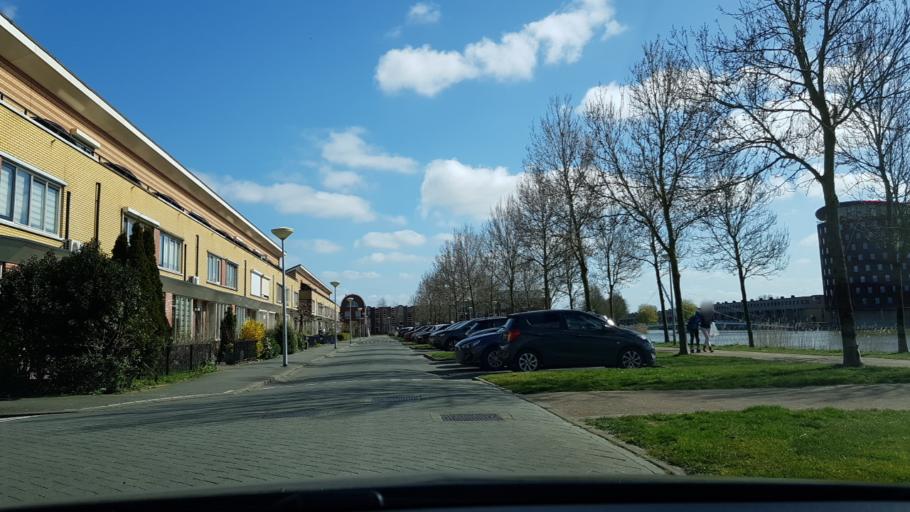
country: NL
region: South Holland
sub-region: Gemeente Hillegom
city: Hillegom
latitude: 52.2693
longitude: 4.6075
